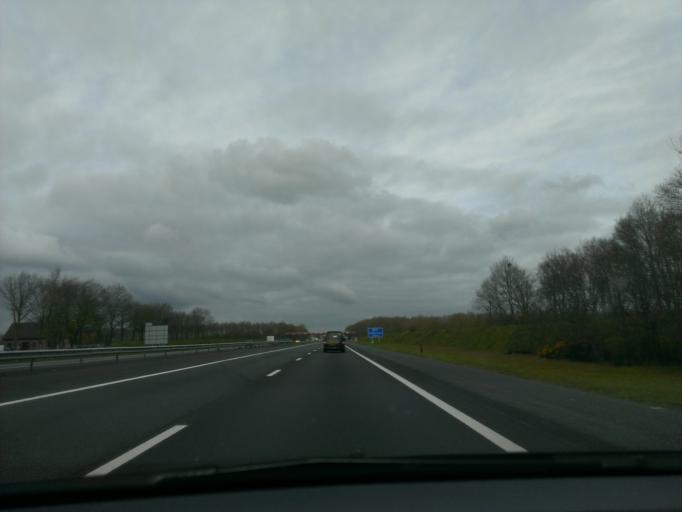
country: NL
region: Overijssel
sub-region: Gemeente Almelo
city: Almelo
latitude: 52.3172
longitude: 6.6785
